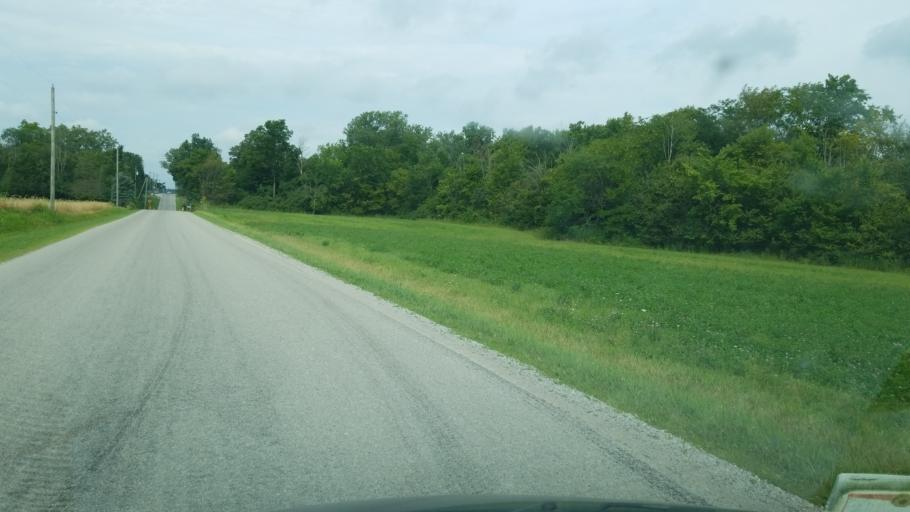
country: US
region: Ohio
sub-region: Sandusky County
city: Green Springs
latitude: 41.1681
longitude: -83.0945
